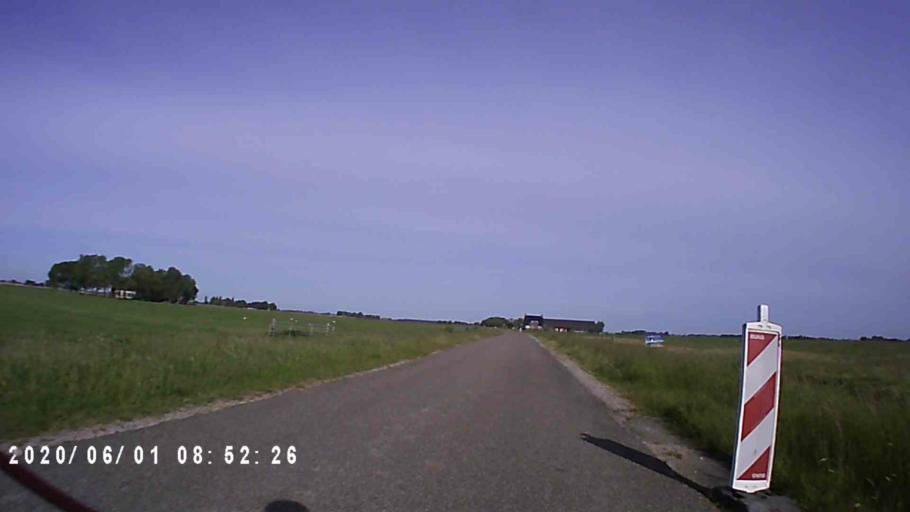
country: NL
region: Friesland
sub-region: Gemeente Ferwerderadiel
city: Burdaard
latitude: 53.2767
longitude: 5.8325
